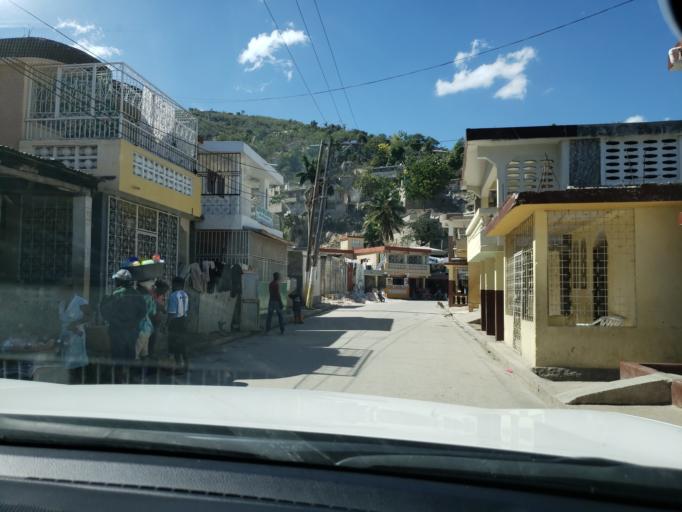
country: HT
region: Nippes
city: Miragoane
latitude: 18.4421
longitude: -73.0913
